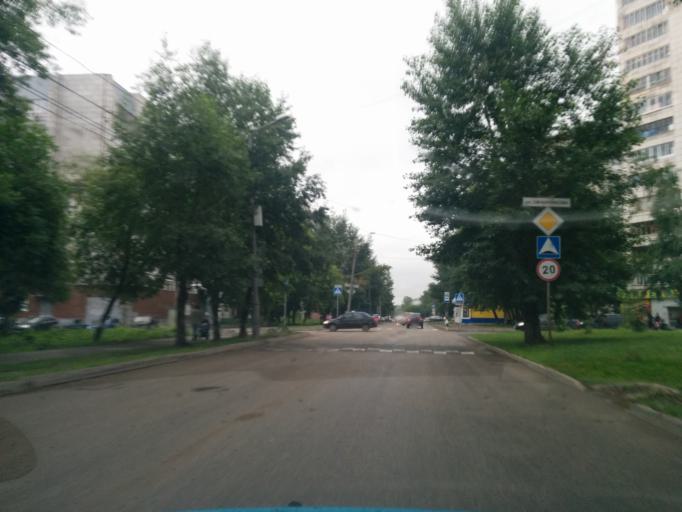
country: RU
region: Perm
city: Perm
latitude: 57.9950
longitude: 56.2278
